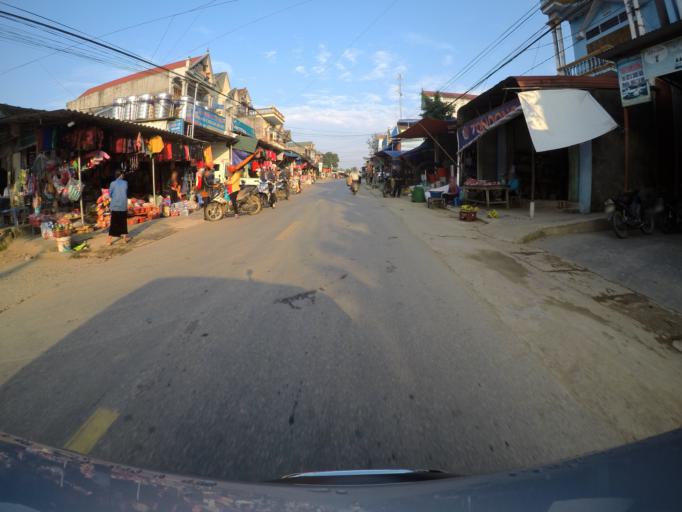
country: VN
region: Lai Chau
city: Tam Duong
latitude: 22.2776
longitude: 103.6818
